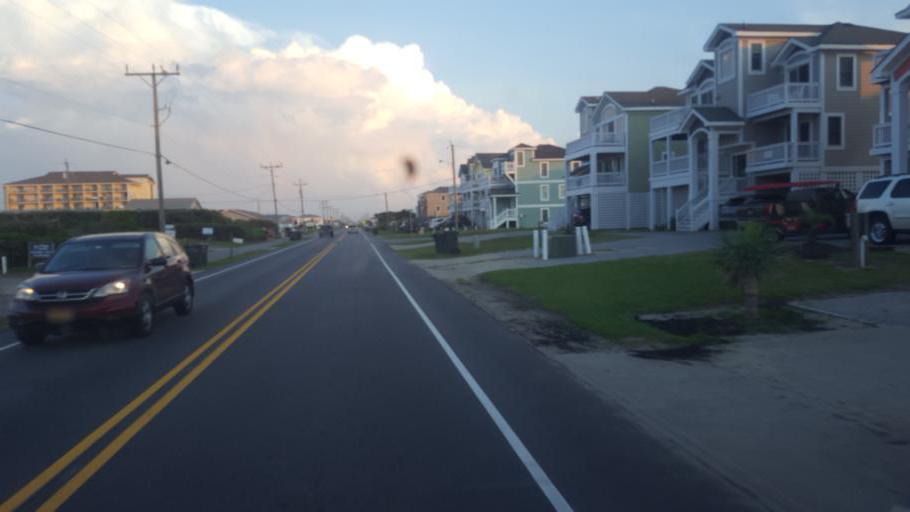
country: US
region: North Carolina
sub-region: Dare County
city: Nags Head
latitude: 35.9214
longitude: -75.6040
